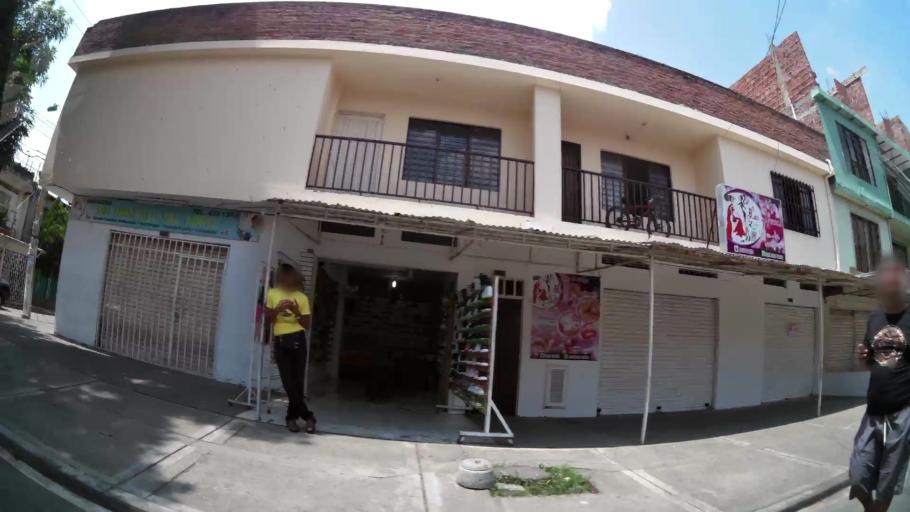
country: CO
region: Valle del Cauca
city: Cali
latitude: 3.4782
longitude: -76.4858
